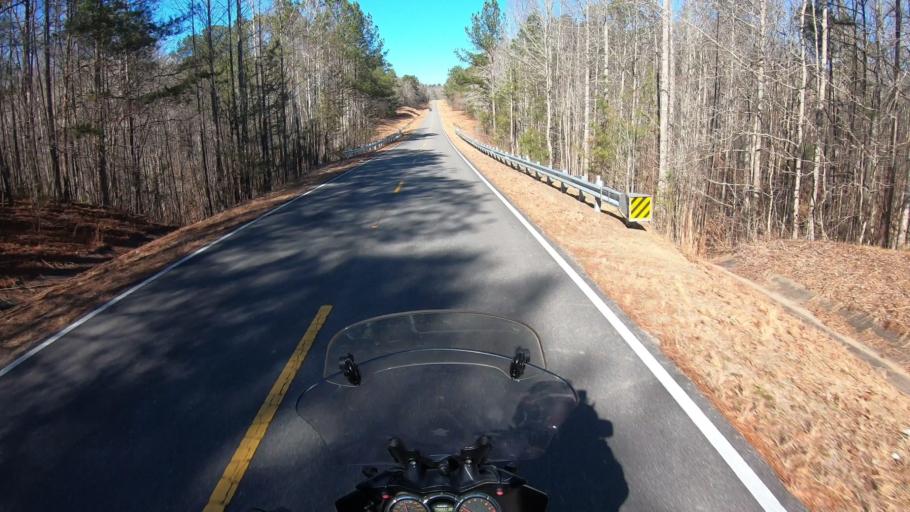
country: US
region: Alabama
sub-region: Calhoun County
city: Choccolocco
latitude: 33.5977
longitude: -85.6767
